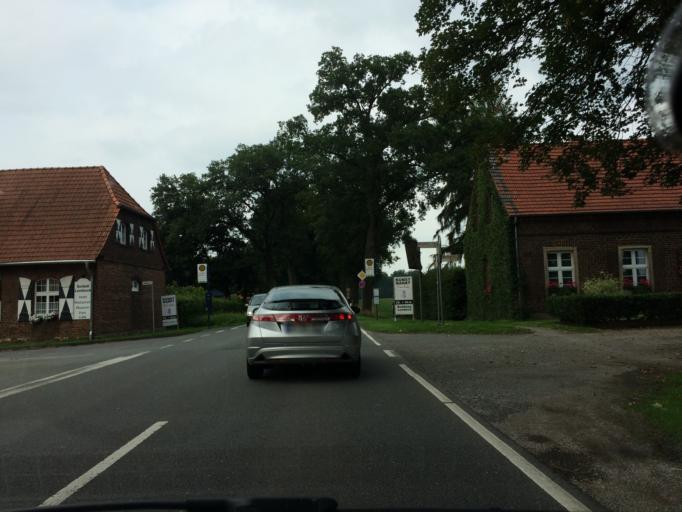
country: DE
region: North Rhine-Westphalia
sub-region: Regierungsbezirk Munster
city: Klein Reken
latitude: 51.7432
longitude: 7.0038
